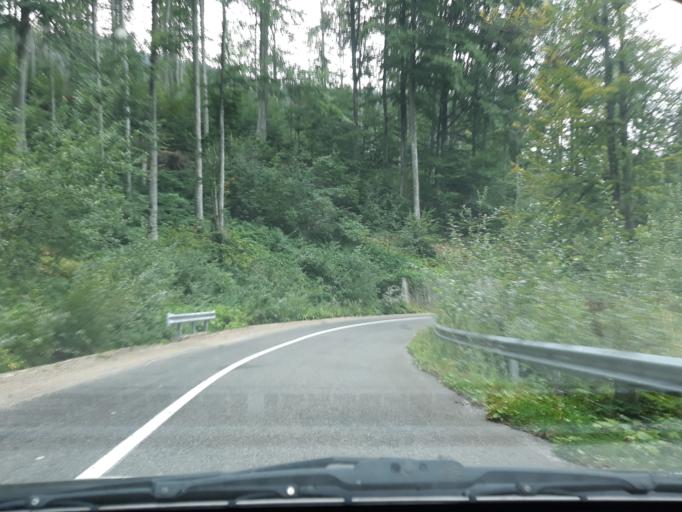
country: RO
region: Bihor
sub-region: Comuna Pietroasa
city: Pietroasa
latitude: 46.5967
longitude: 22.6586
